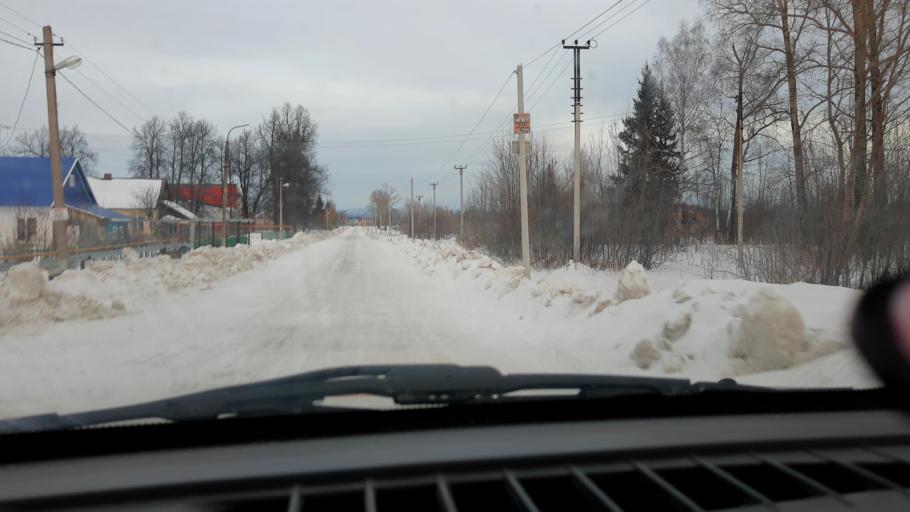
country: RU
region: Bashkortostan
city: Urman
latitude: 54.8650
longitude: 56.8550
